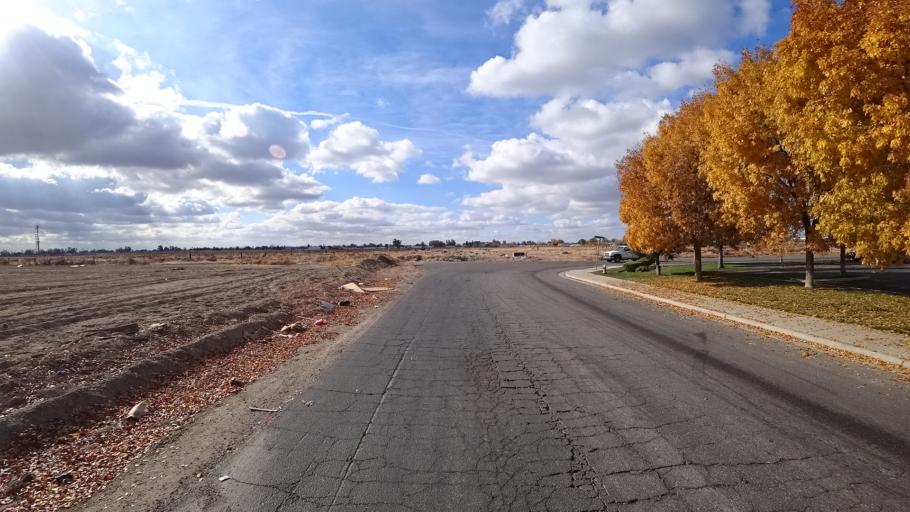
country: US
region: California
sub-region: Kern County
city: Bakersfield
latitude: 35.3468
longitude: -118.9762
